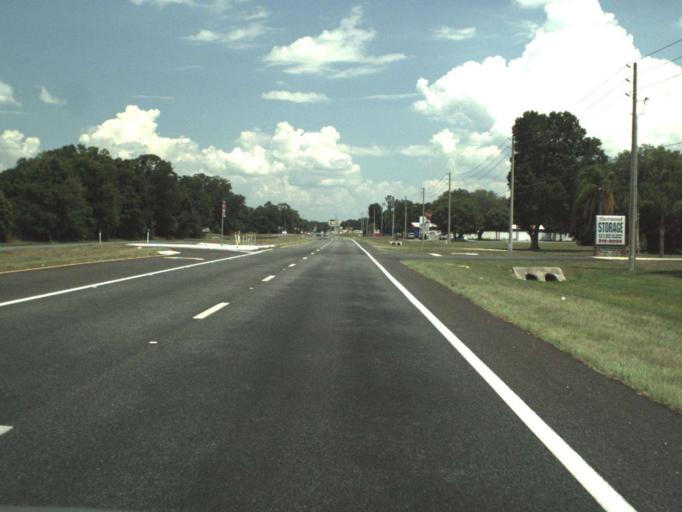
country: US
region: Florida
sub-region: Lake County
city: Fruitland Park
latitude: 28.8144
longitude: -81.9346
